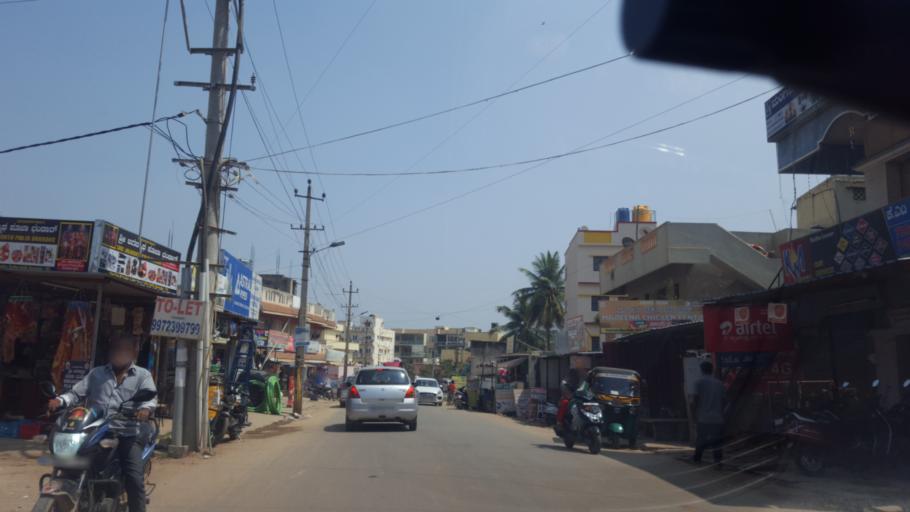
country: IN
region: Karnataka
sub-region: Bangalore Urban
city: Bangalore
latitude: 12.9366
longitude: 77.7040
